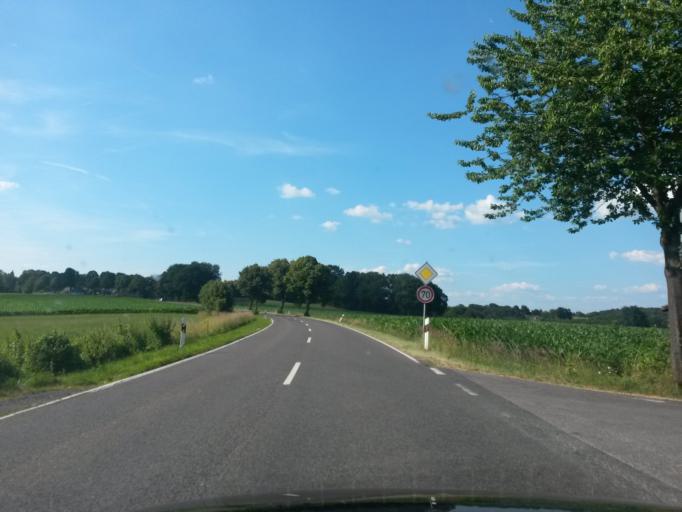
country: DE
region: North Rhine-Westphalia
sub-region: Regierungsbezirk Koln
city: Much
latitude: 50.8947
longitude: 7.3426
